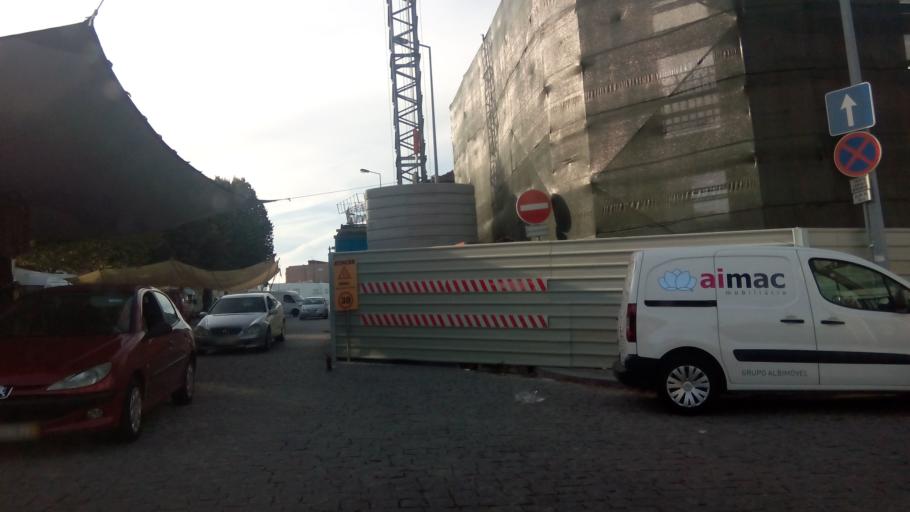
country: PT
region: Porto
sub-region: Paredes
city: Paredes
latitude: 41.2054
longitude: -8.3298
